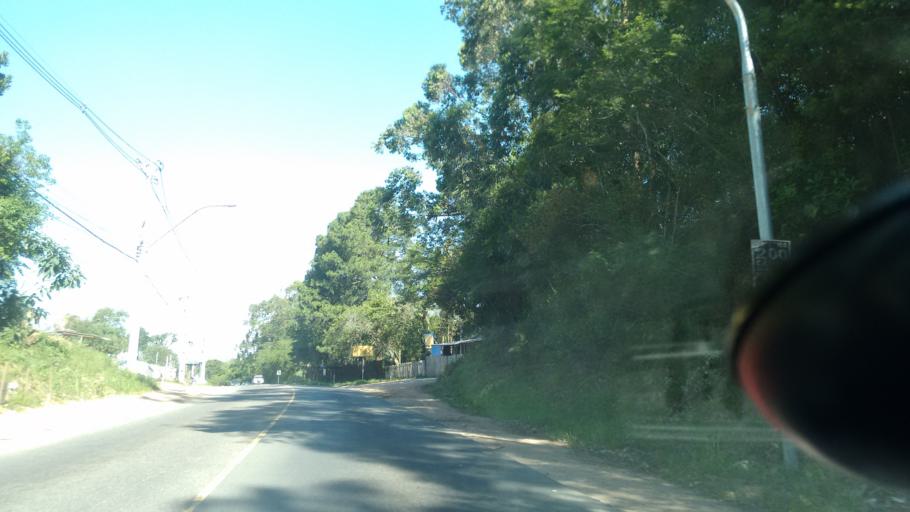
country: BR
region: Rio Grande do Sul
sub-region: Cachoeirinha
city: Cachoeirinha
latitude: -30.0402
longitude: -51.1091
